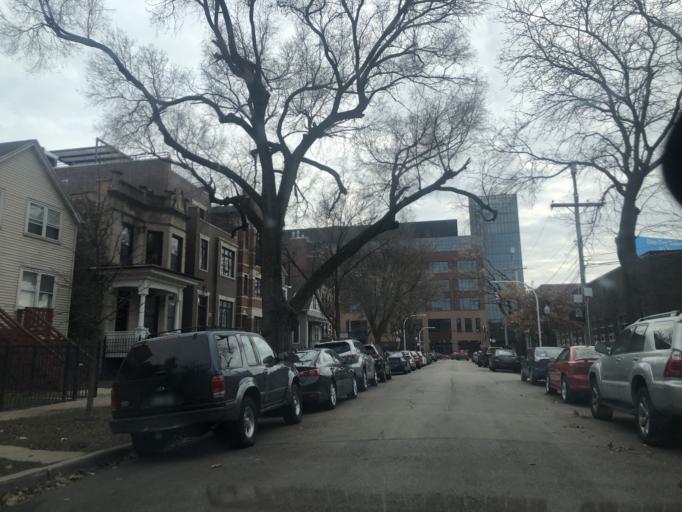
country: US
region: Illinois
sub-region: Cook County
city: Lincolnwood
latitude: 41.9502
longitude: -87.6575
